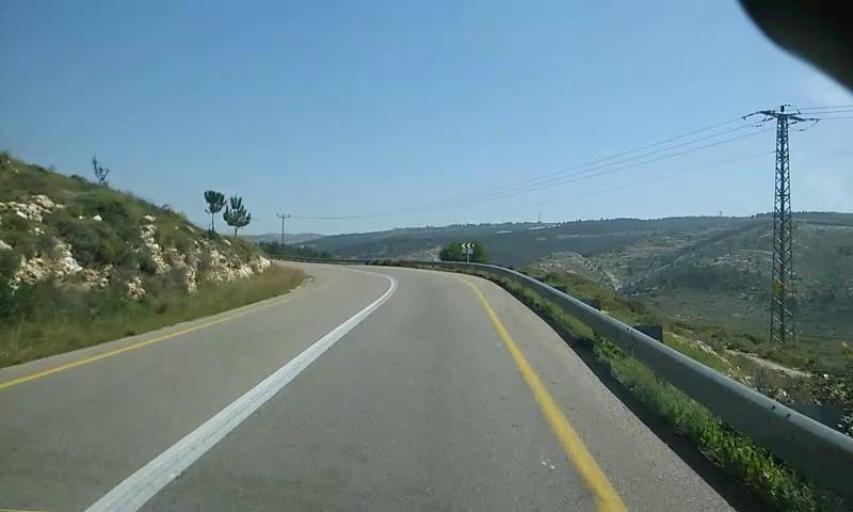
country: PS
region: West Bank
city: Surif
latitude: 31.6728
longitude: 35.0871
